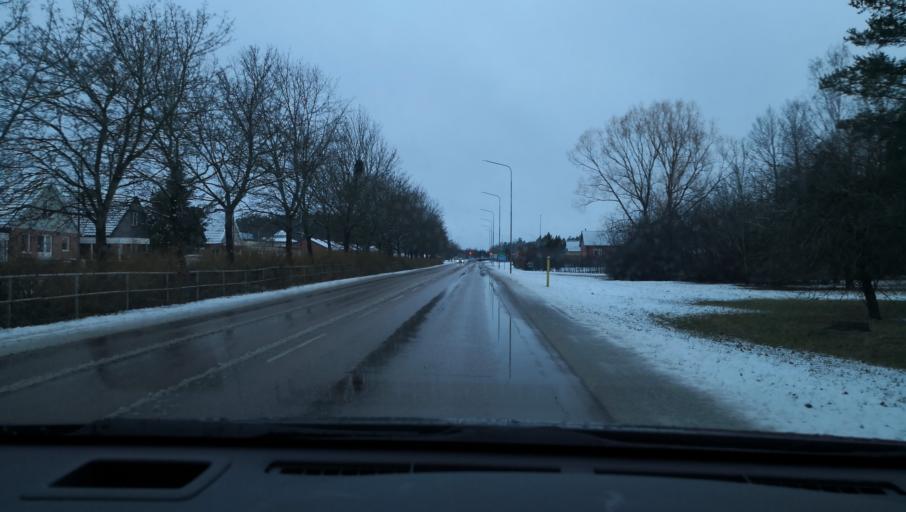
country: SE
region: Vaestmanland
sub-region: Kopings Kommun
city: Koping
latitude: 59.5182
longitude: 16.0092
